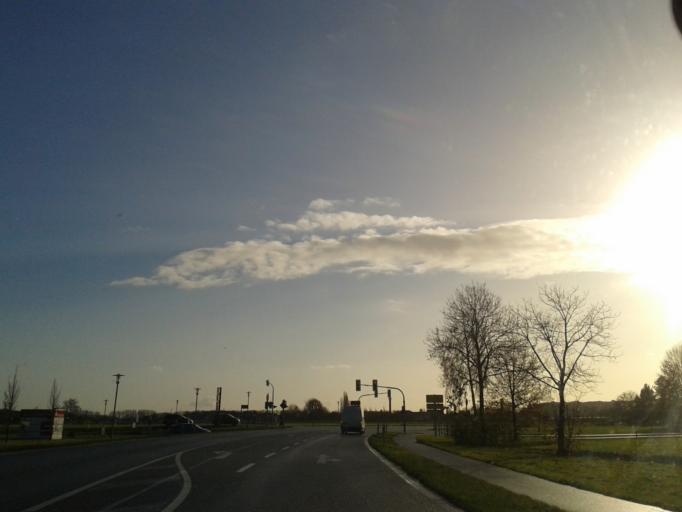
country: DE
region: North Rhine-Westphalia
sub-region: Regierungsbezirk Dusseldorf
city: Xanten
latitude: 51.6693
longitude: 6.4533
